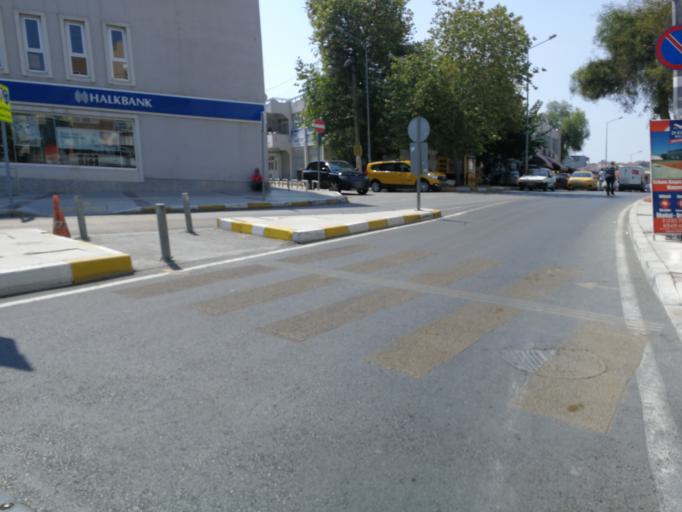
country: TR
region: Izmir
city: Urla
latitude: 38.3250
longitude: 26.7667
